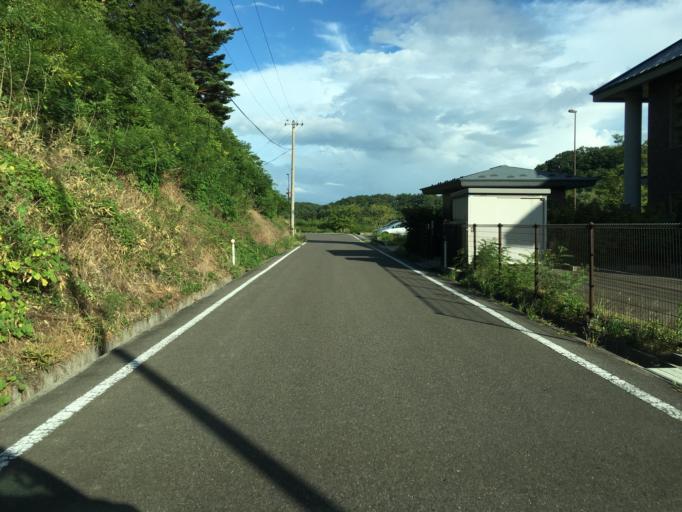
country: JP
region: Fukushima
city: Nihommatsu
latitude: 37.6321
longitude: 140.4180
